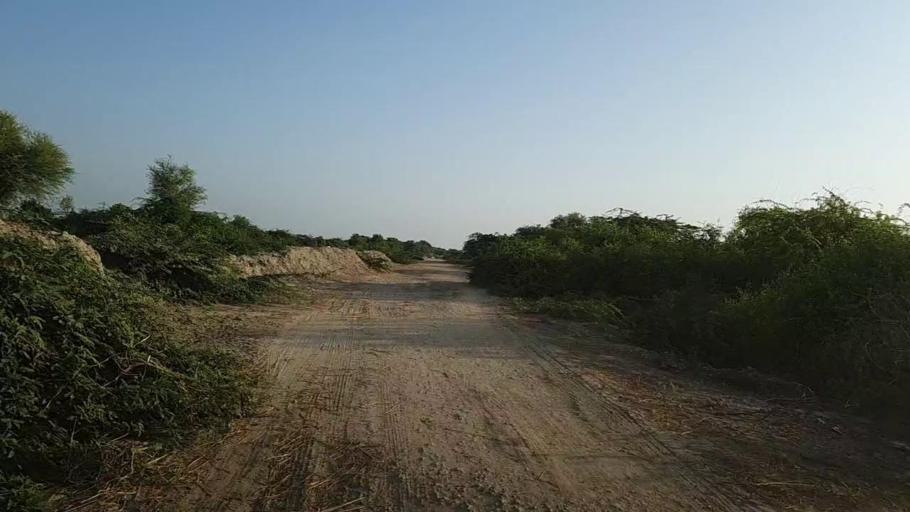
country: PK
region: Sindh
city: Kario
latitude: 24.7191
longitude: 68.6673
